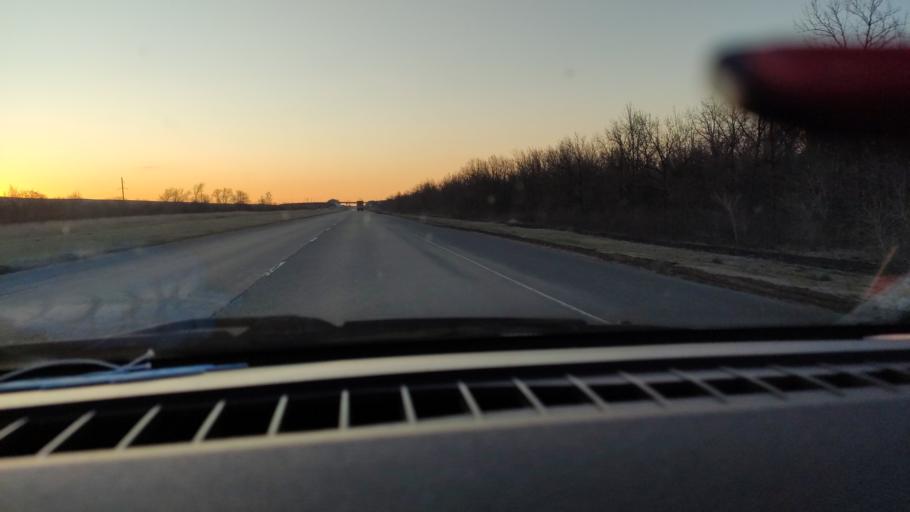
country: RU
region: Saratov
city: Yelshanka
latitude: 51.8270
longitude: 46.2761
